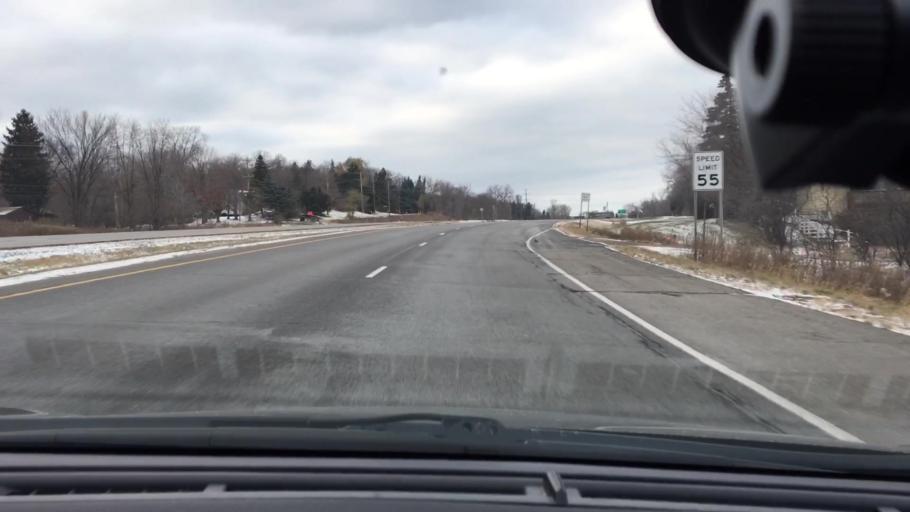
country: US
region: Minnesota
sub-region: Hennepin County
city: Plymouth
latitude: 44.9911
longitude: -93.4318
